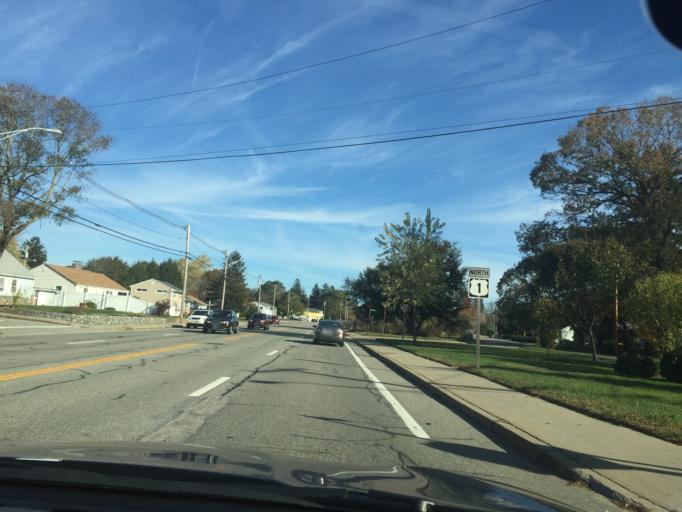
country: US
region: Rhode Island
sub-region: Kent County
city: East Greenwich
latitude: 41.6439
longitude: -71.4648
